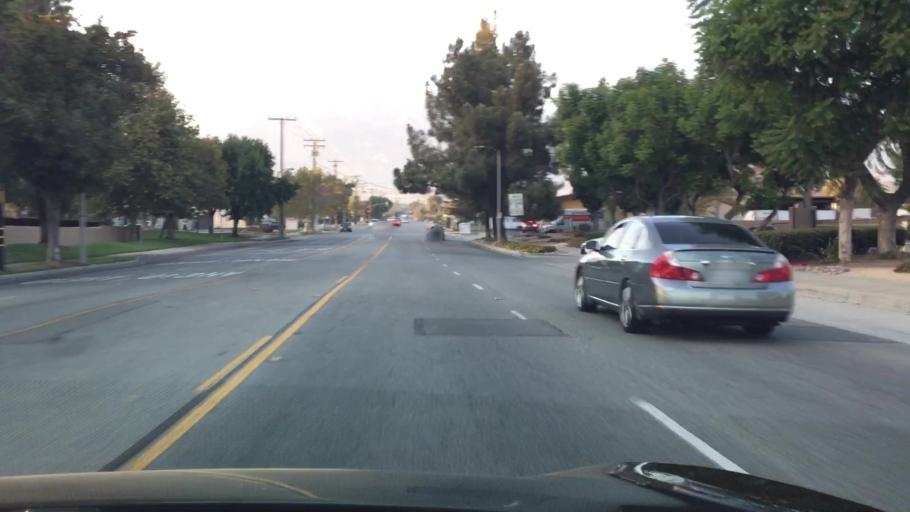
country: US
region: California
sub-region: San Bernardino County
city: Upland
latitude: 34.0930
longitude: -117.6286
